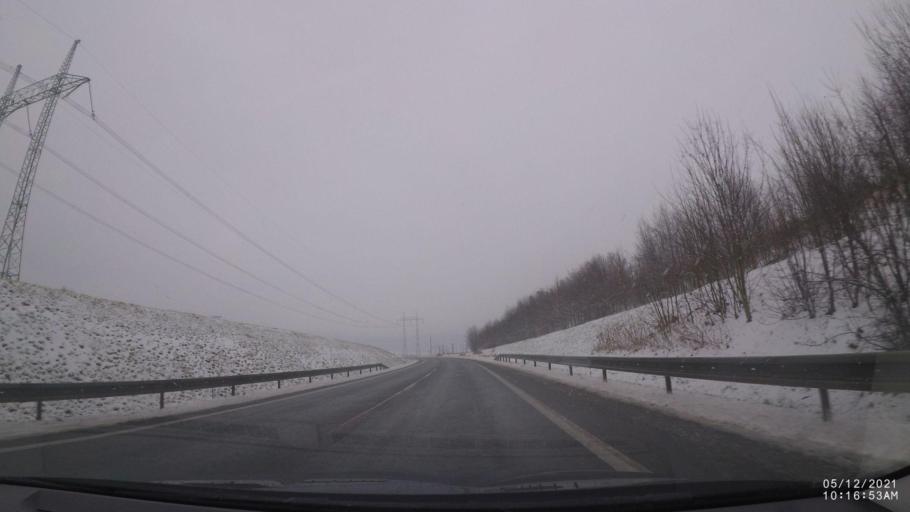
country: CZ
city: Vamberk
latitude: 50.1095
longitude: 16.2823
